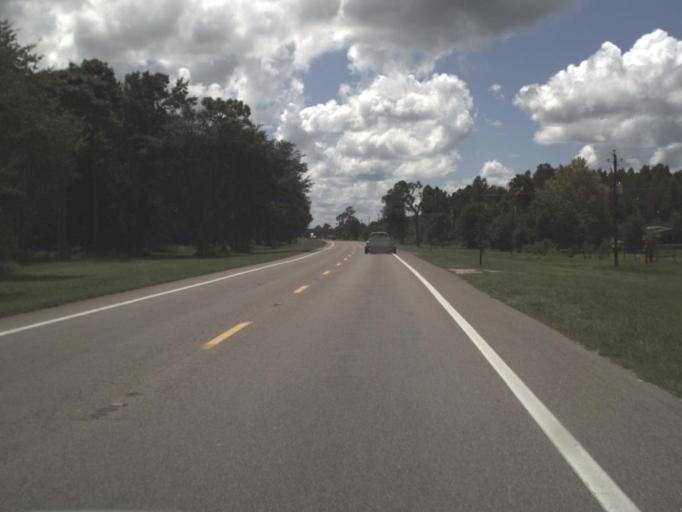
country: US
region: Florida
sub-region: Polk County
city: Polk City
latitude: 28.2673
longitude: -81.8278
